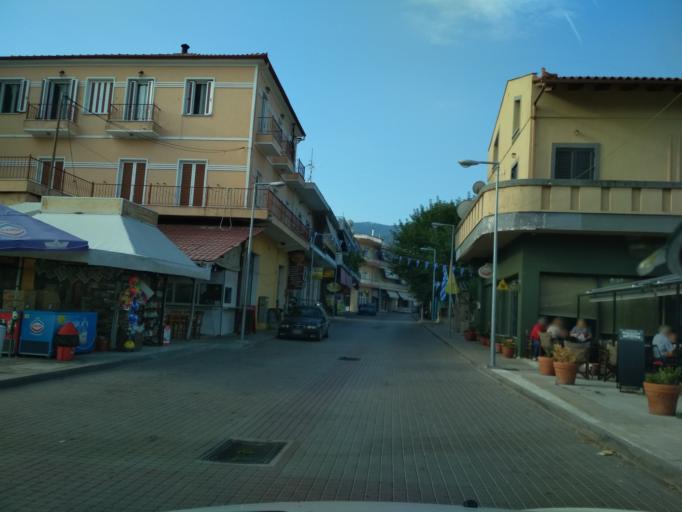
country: GR
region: Central Greece
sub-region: Nomos Evvoias
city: Prokopion
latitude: 38.7348
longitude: 23.4928
